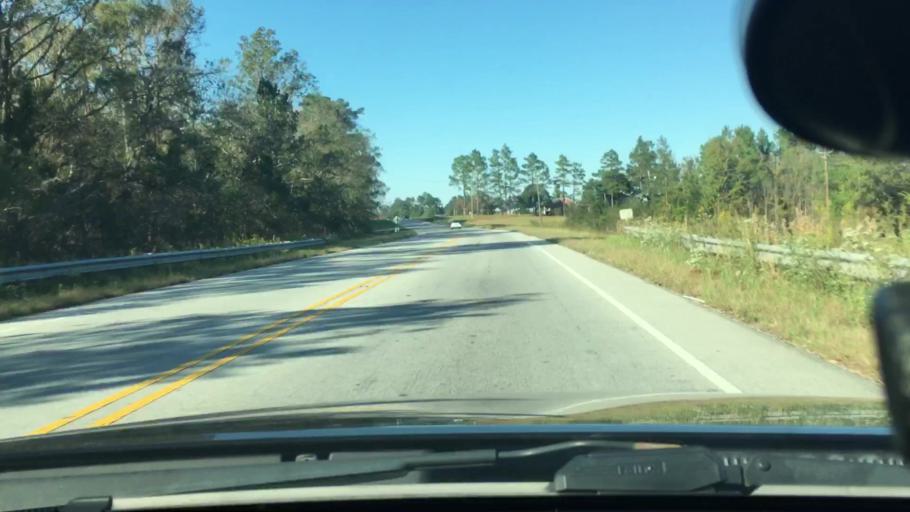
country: US
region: North Carolina
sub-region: Craven County
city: Trent Woods
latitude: 35.1789
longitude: -77.1315
